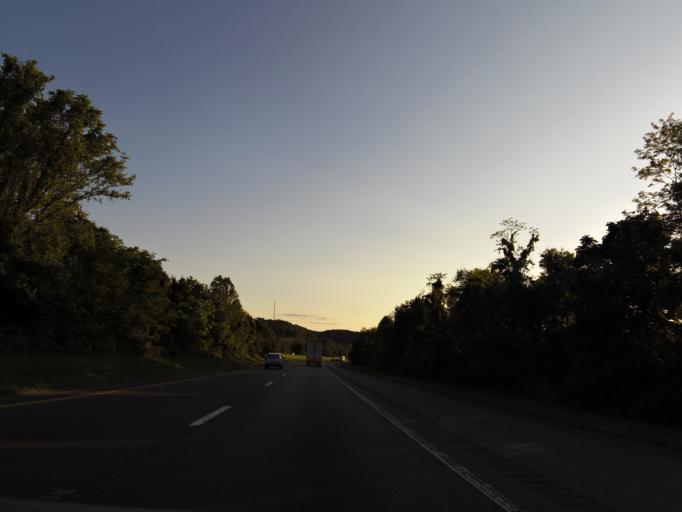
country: US
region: Tennessee
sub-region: Washington County
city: Fall Branch
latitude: 36.4057
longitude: -82.6059
